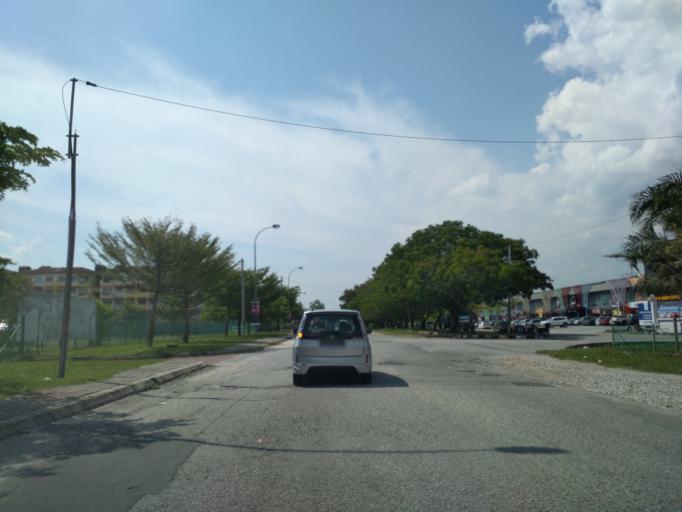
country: MY
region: Perak
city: Kampar
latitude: 4.3284
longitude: 101.1463
